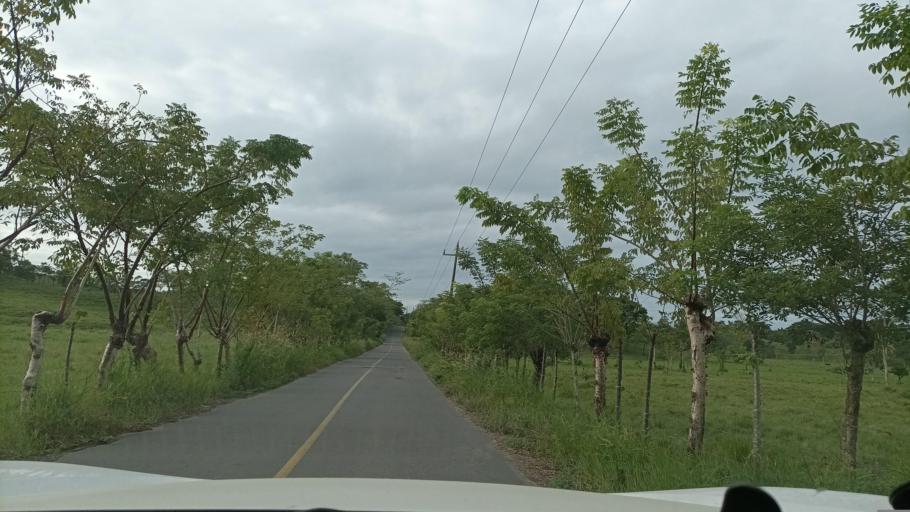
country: MX
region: Veracruz
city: Hidalgotitlan
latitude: 17.7019
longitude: -94.4673
